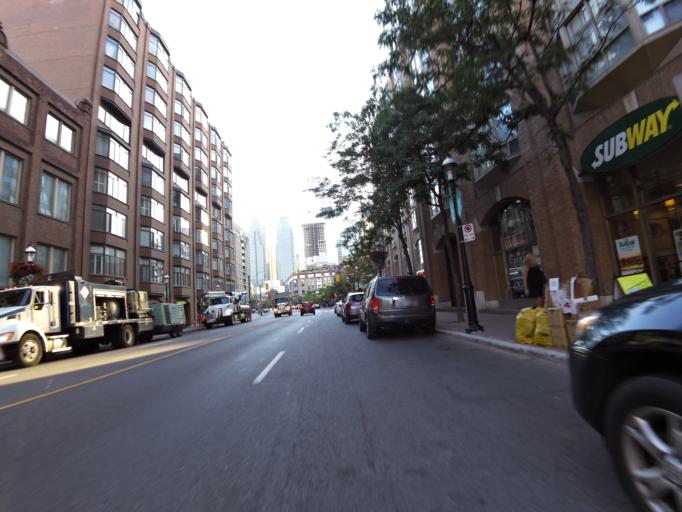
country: CA
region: Ontario
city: Toronto
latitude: 43.6501
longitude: -79.3693
